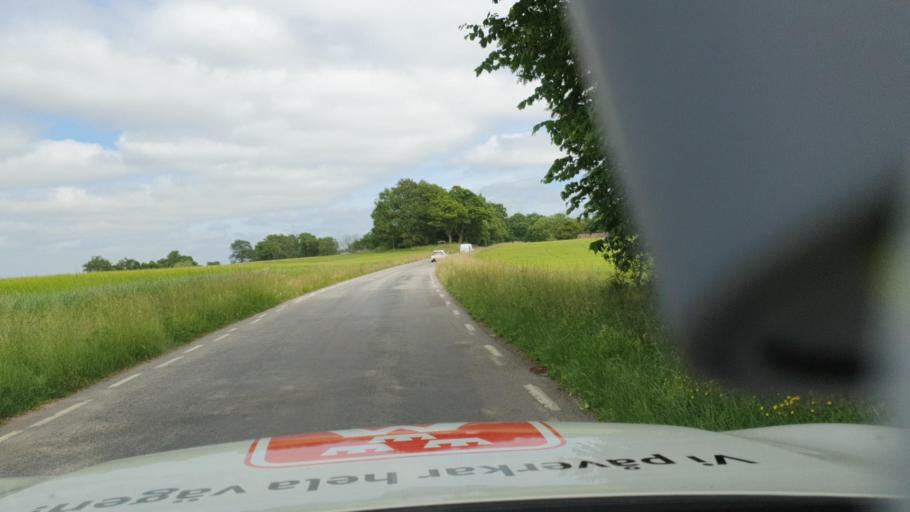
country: SE
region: Vaestra Goetaland
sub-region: Gotene Kommun
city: Goetene
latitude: 58.5753
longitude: 13.4124
